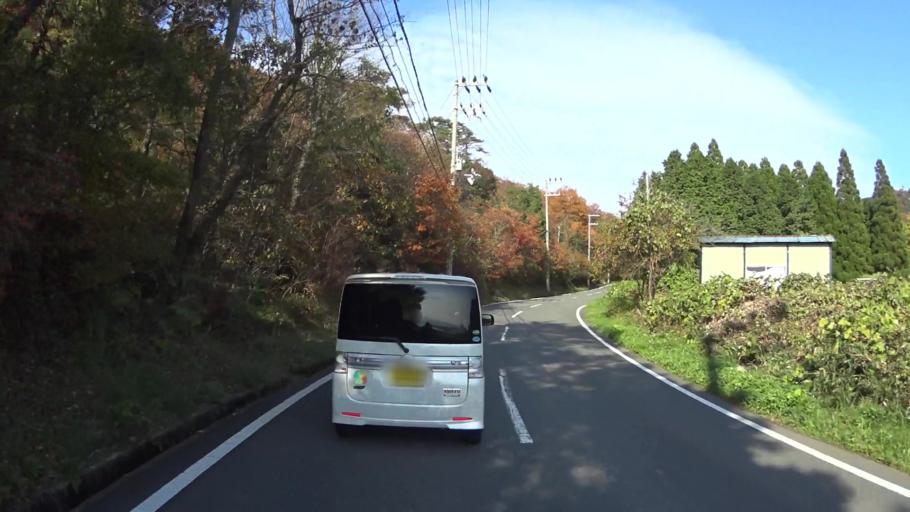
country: JP
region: Kyoto
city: Maizuru
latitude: 35.5295
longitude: 135.3928
